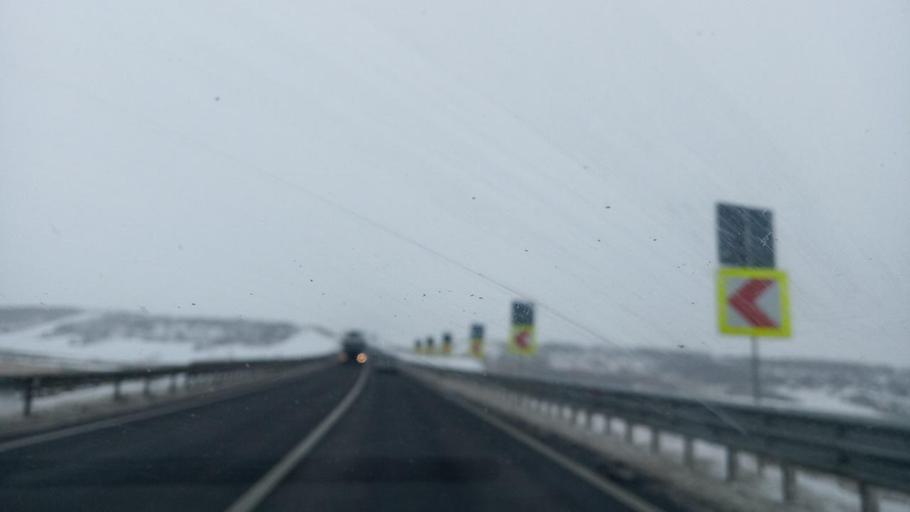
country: RO
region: Bacau
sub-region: Comuna Saucesti
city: Saucesti
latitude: 46.6380
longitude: 26.9271
